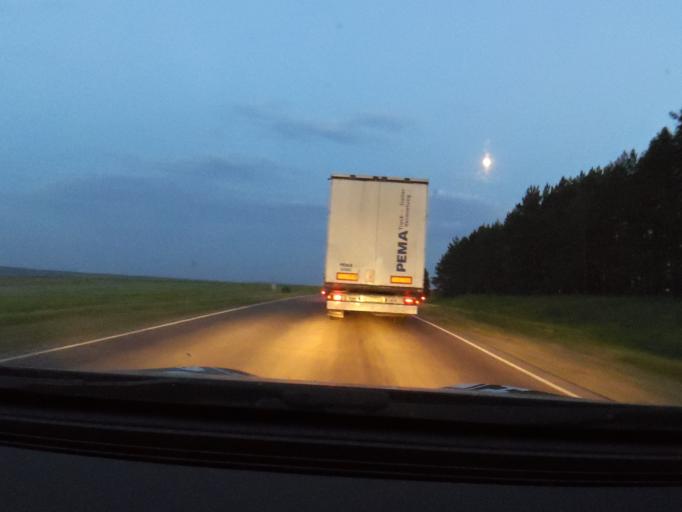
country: RU
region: Bashkortostan
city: Duvan
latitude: 56.0453
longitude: 58.2039
